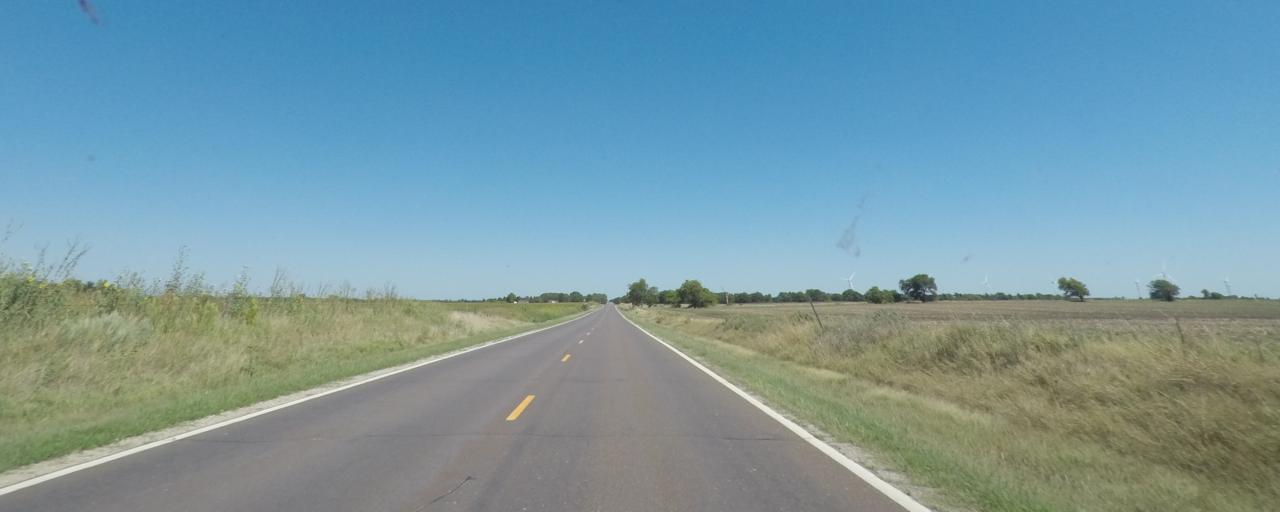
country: US
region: Kansas
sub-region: Sumner County
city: Wellington
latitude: 37.1199
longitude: -97.4017
